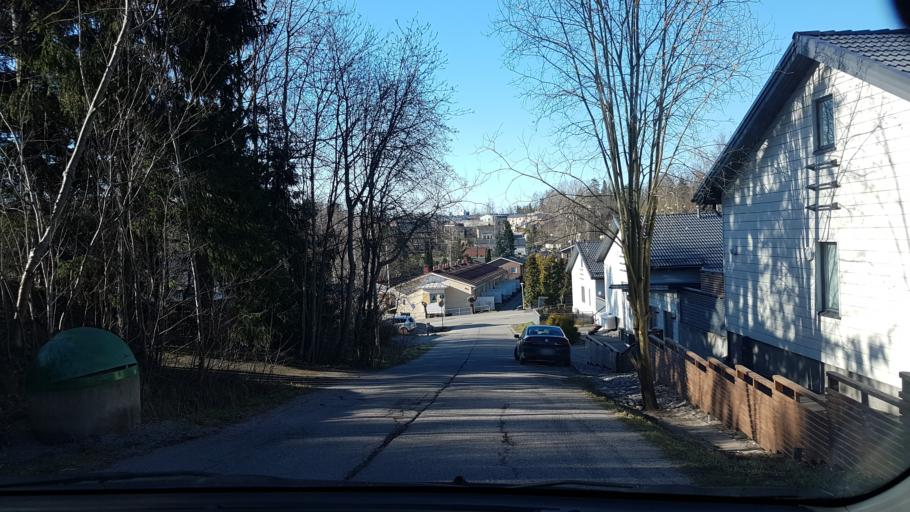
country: FI
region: Uusimaa
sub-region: Helsinki
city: Vantaa
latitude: 60.2692
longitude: 25.0924
